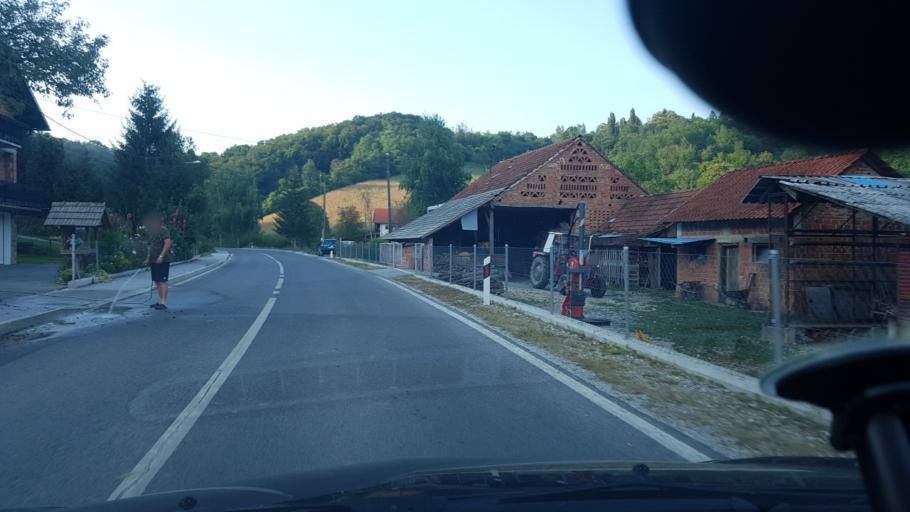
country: HR
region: Krapinsko-Zagorska
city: Pregrada
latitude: 46.1493
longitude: 15.7937
